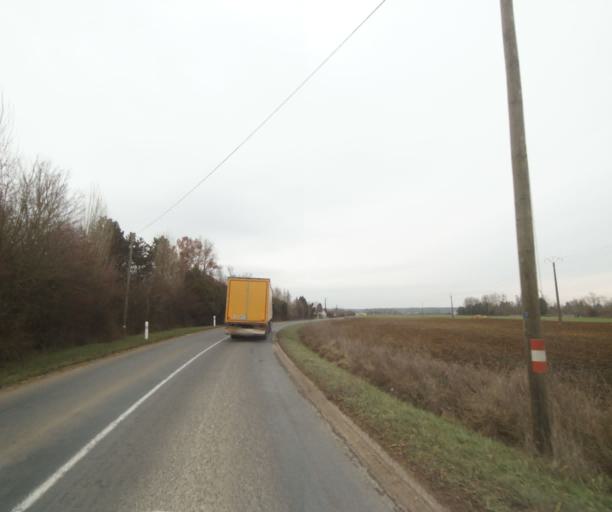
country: FR
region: Champagne-Ardenne
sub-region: Departement de la Haute-Marne
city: Villiers-en-Lieu
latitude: 48.6496
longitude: 4.9063
